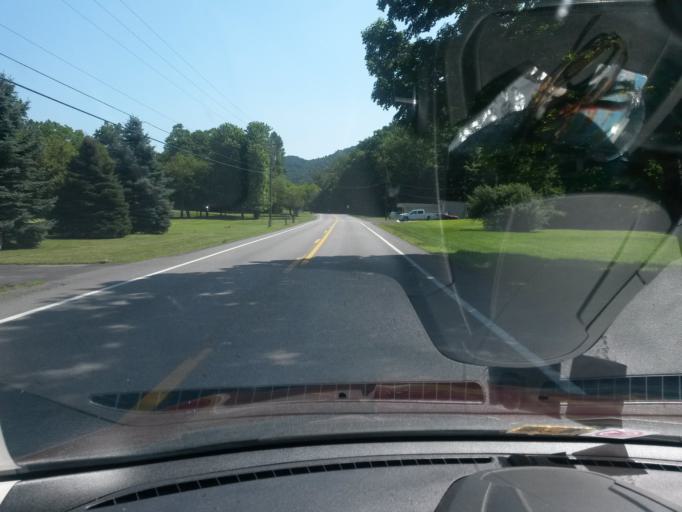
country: US
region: West Virginia
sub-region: Mineral County
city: Keyser
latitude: 39.3434
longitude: -79.0650
